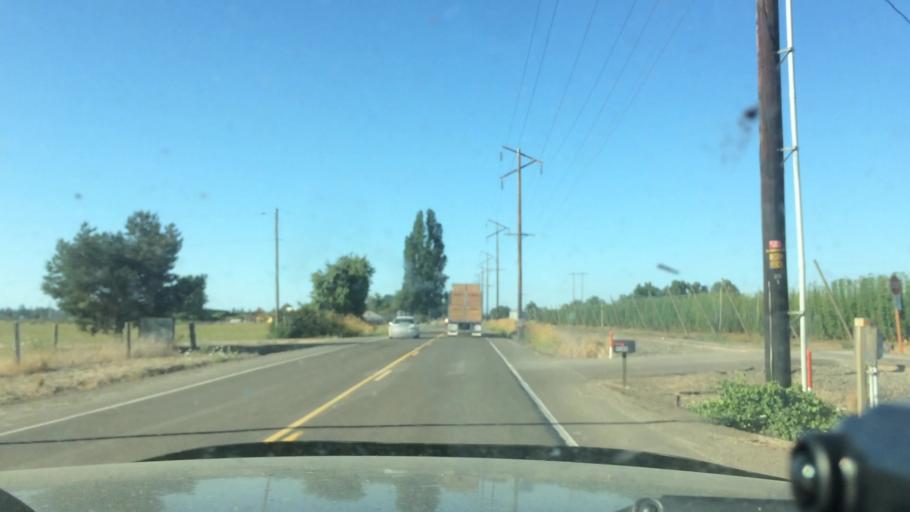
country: US
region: Oregon
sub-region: Marion County
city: Hayesville
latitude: 45.0566
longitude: -122.9841
